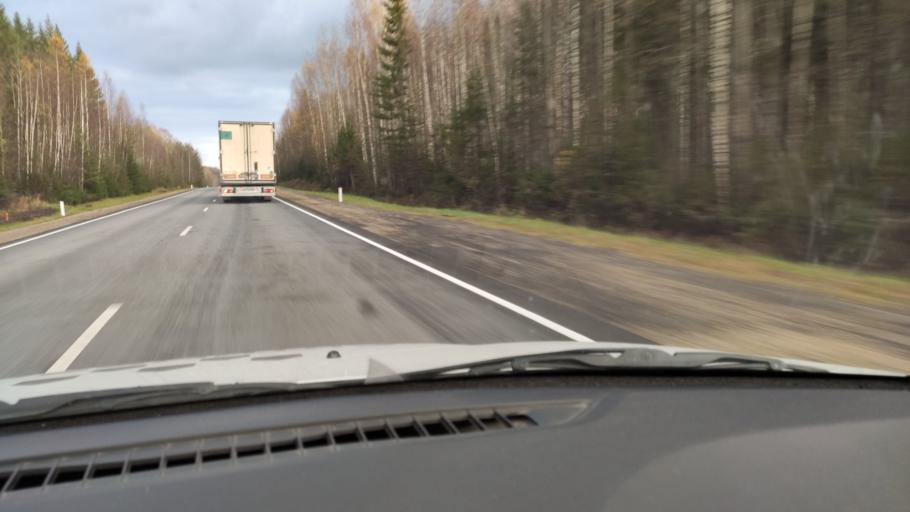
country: RU
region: Kirov
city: Chernaya Kholunitsa
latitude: 58.7746
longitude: 51.9347
